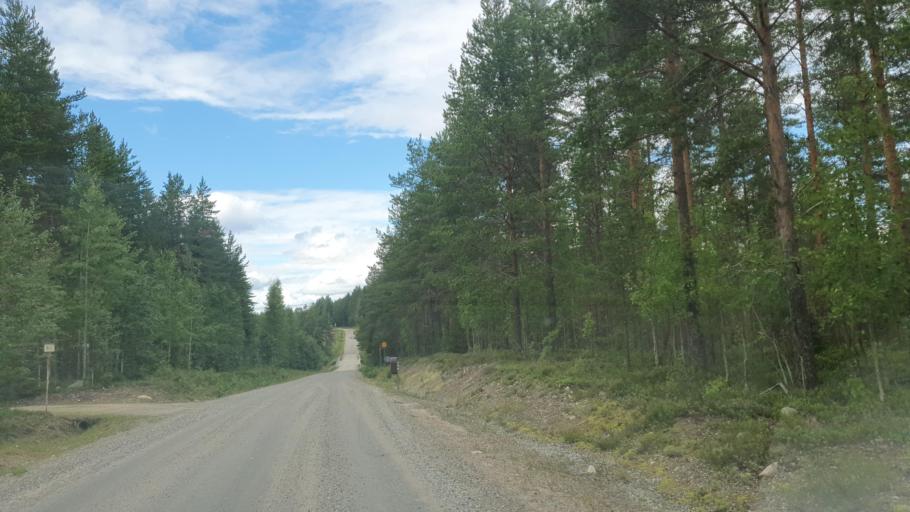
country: FI
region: Kainuu
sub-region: Kehys-Kainuu
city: Kuhmo
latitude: 64.1077
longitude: 29.3894
